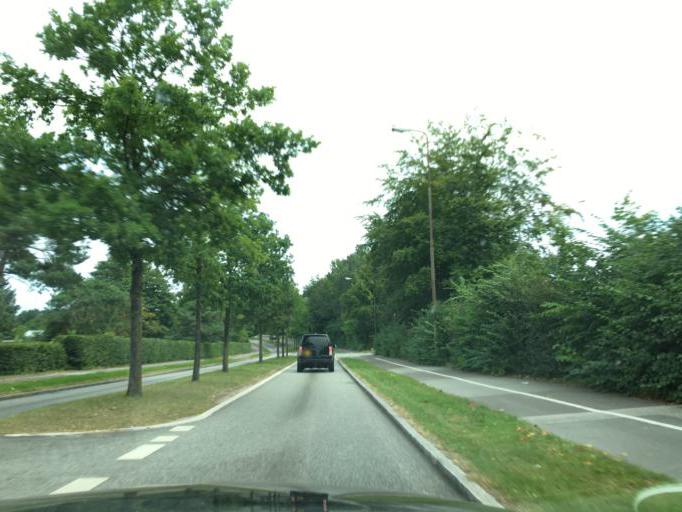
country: DK
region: Capital Region
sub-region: Horsholm Kommune
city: Horsholm
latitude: 55.8924
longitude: 12.4970
